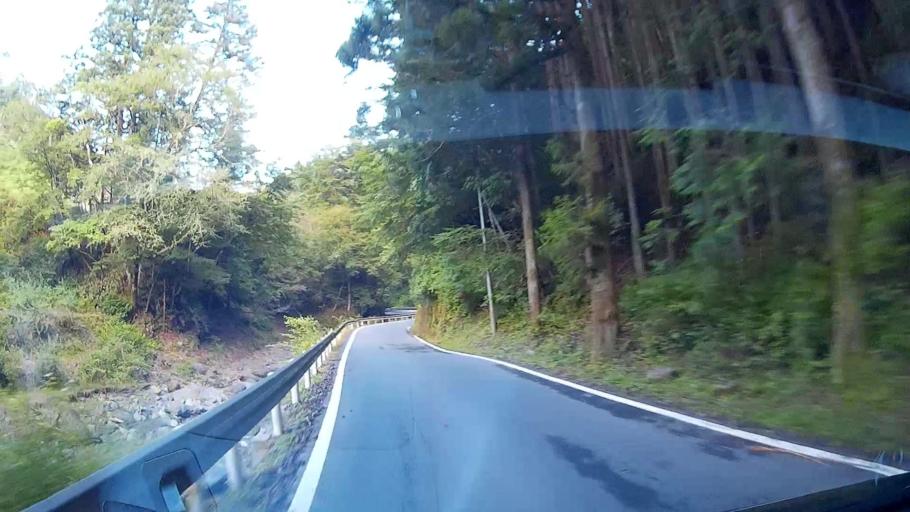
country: JP
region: Shizuoka
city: Shizuoka-shi
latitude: 35.1519
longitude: 138.2576
